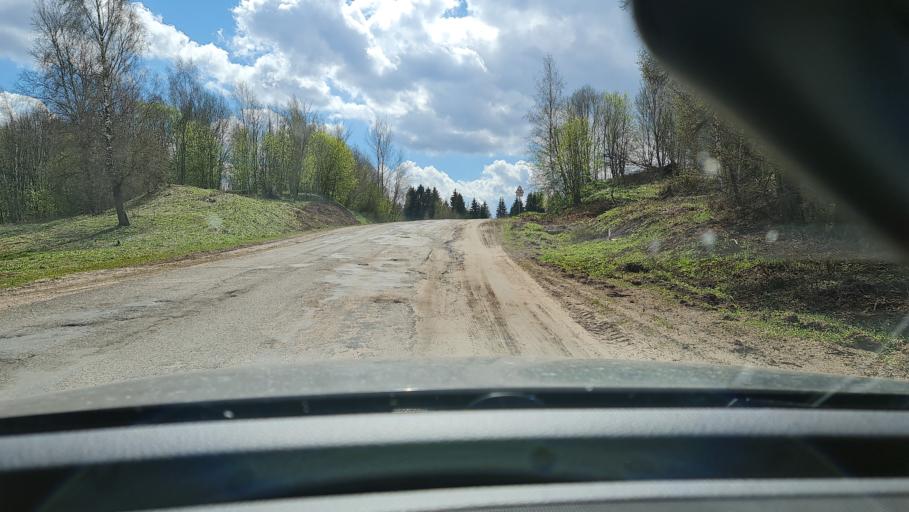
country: RU
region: Tverskaya
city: Toropets
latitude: 56.6423
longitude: 31.4215
